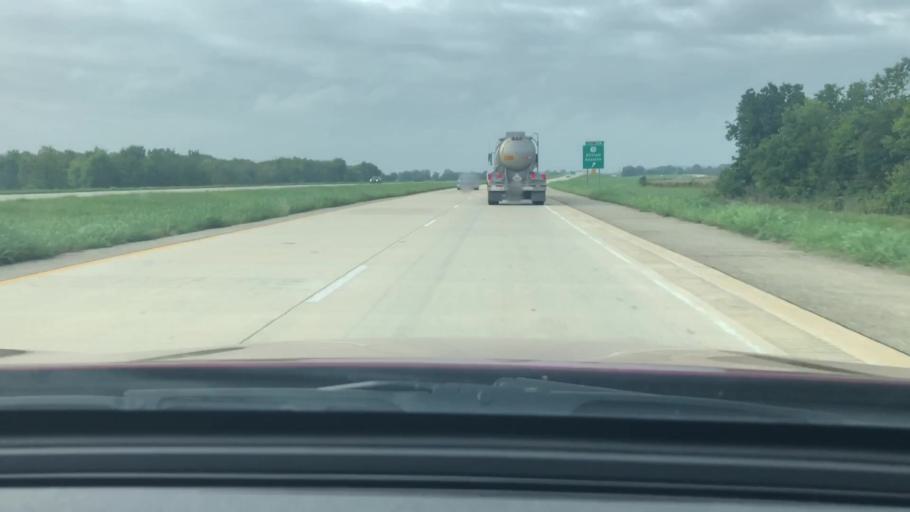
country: US
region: Louisiana
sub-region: Caddo Parish
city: Vivian
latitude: 32.8587
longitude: -93.8618
